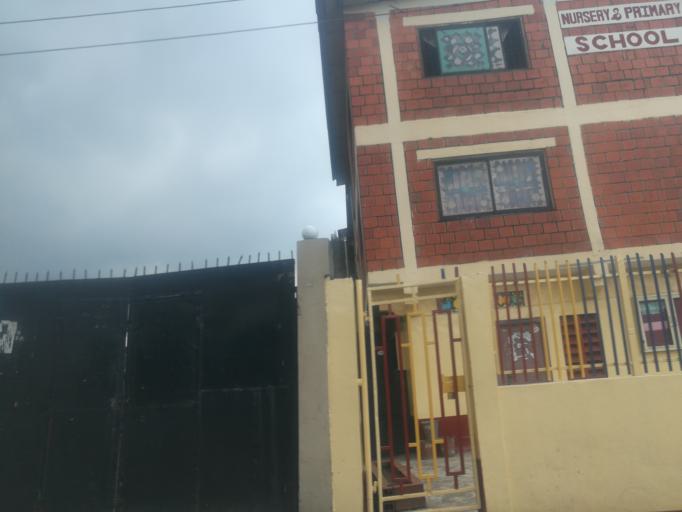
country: NG
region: Lagos
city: Ojota
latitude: 6.5918
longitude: 3.3863
